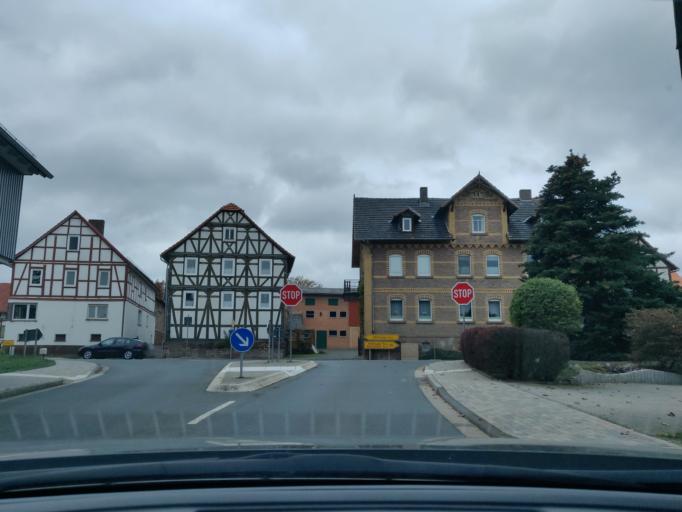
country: DE
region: Hesse
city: Fritzlar
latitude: 51.1792
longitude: 9.2670
